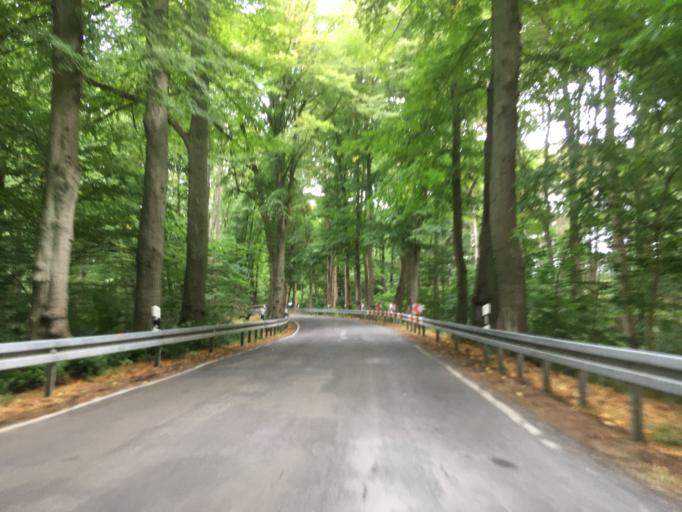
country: DE
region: Brandenburg
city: Mittenwalde
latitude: 53.2443
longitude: 13.5940
